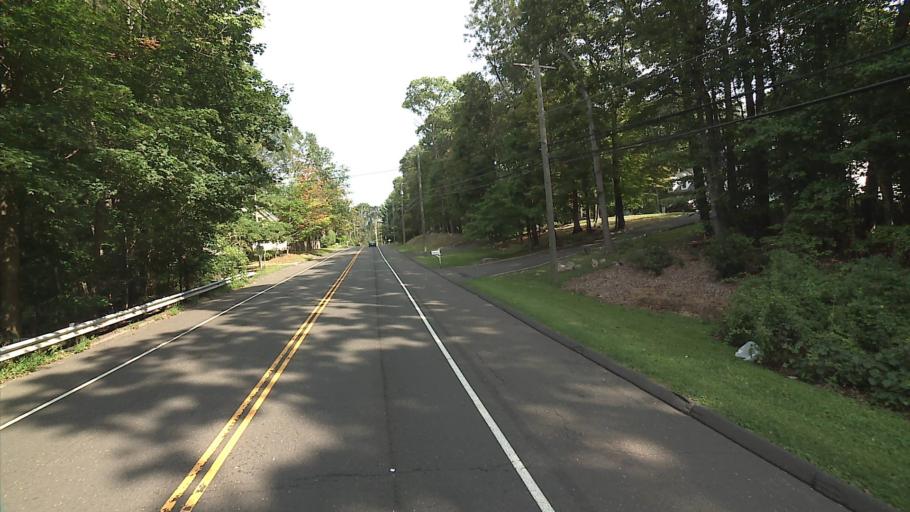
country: US
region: Connecticut
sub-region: Fairfield County
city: New Canaan
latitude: 41.1619
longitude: -73.4947
